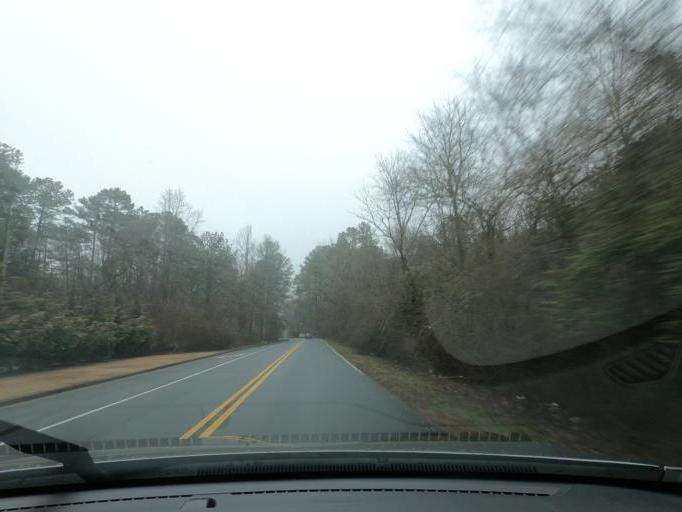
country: US
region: Georgia
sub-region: Fulton County
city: Milton
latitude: 34.1078
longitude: -84.3184
